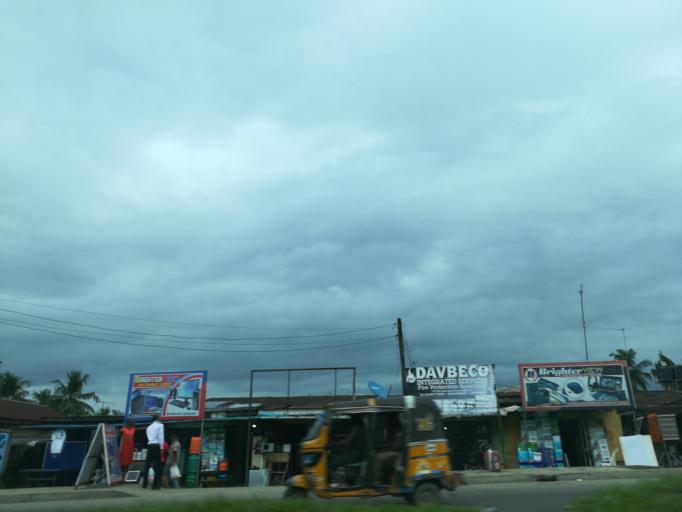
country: NG
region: Rivers
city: Port Harcourt
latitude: 4.8402
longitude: 7.0396
